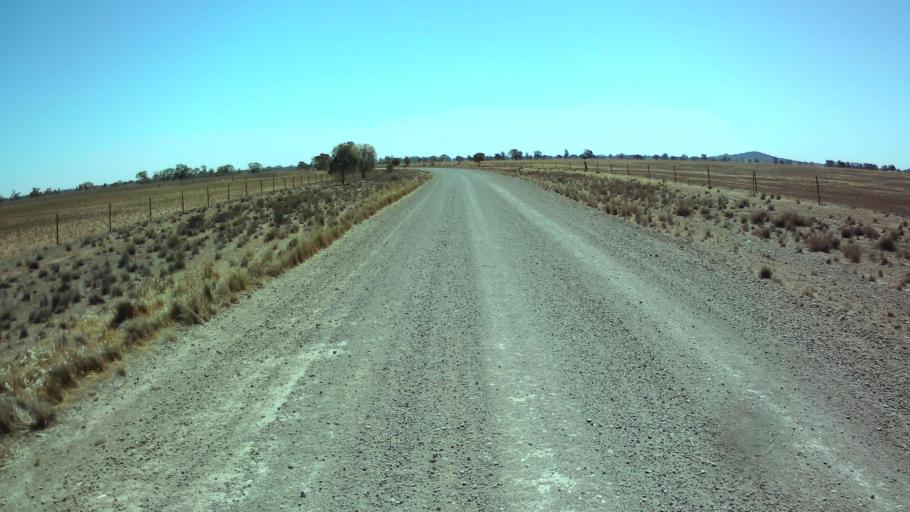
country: AU
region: New South Wales
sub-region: Forbes
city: Forbes
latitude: -33.7458
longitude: 147.7324
